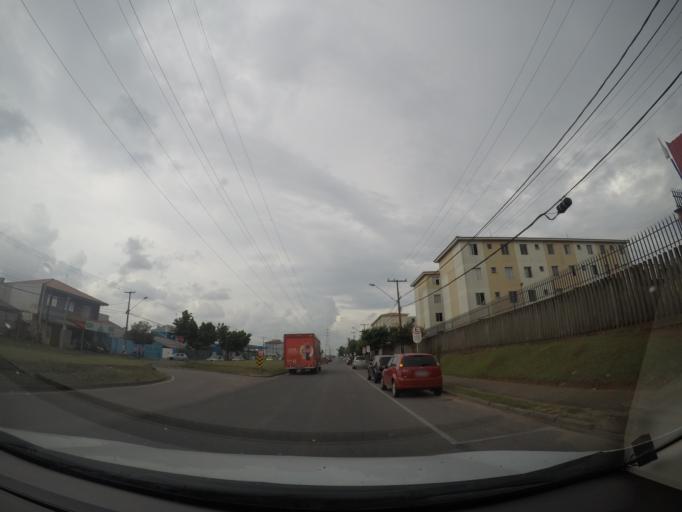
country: BR
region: Parana
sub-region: Sao Jose Dos Pinhais
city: Sao Jose dos Pinhais
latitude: -25.5455
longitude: -49.2647
